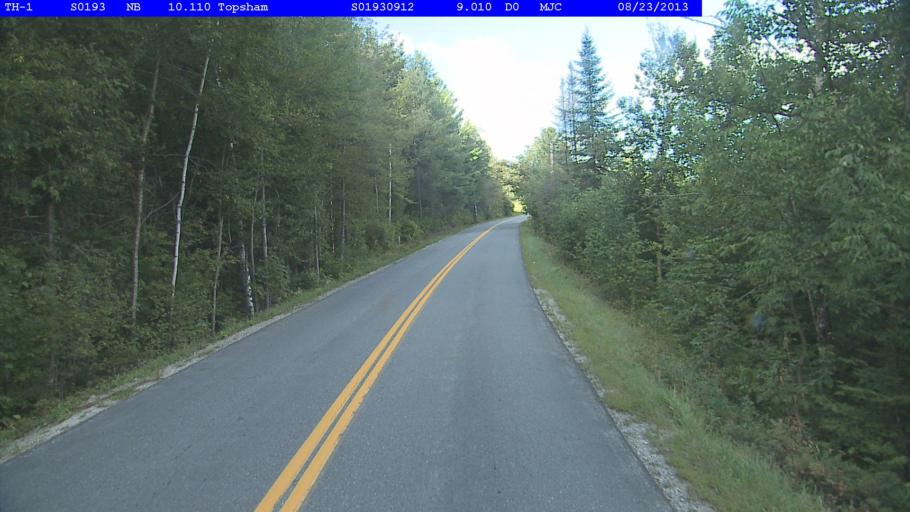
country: US
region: New Hampshire
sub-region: Grafton County
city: Woodsville
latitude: 44.1879
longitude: -72.2221
